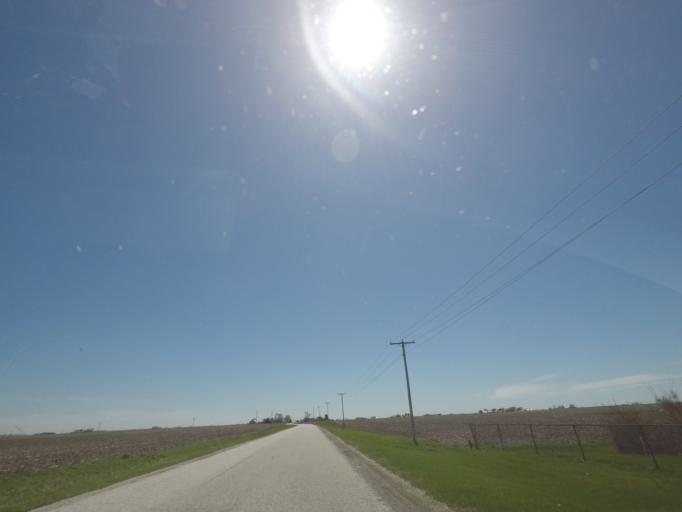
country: US
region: Illinois
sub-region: Logan County
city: Mount Pulaski
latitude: 40.0512
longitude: -89.1824
